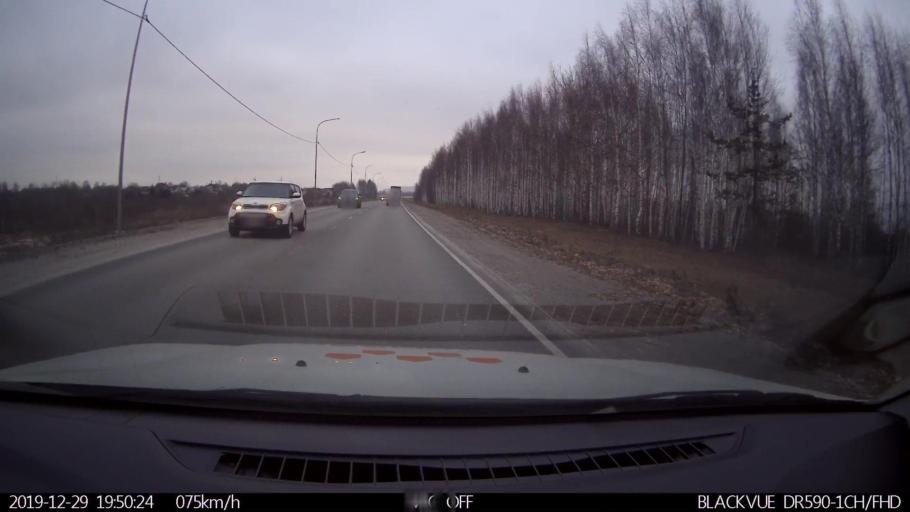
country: RU
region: Nizjnij Novgorod
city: Nizhniy Novgorod
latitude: 56.3686
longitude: 44.0277
